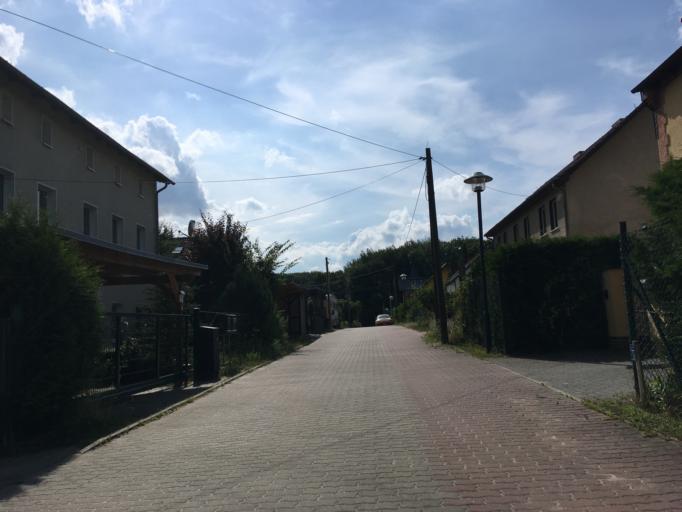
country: DE
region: Brandenburg
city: Rudnitz
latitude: 52.7562
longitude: 13.5673
